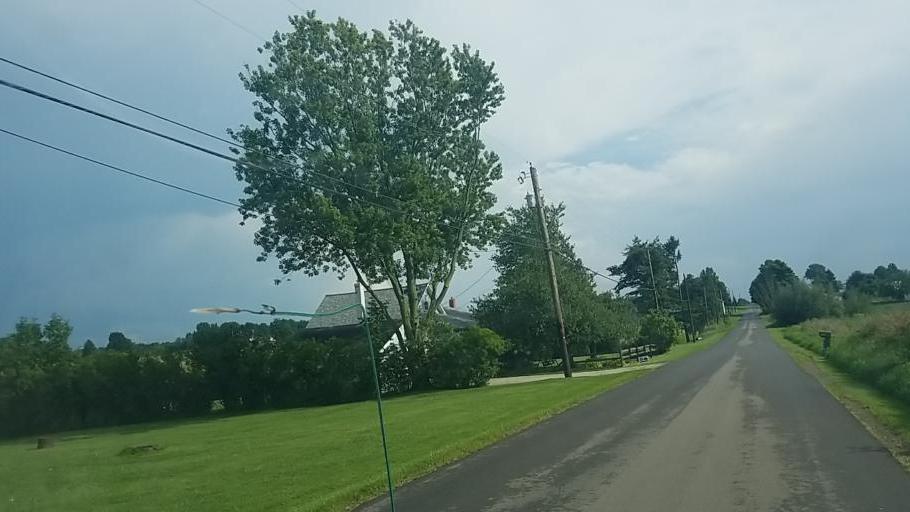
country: US
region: Ohio
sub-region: Wayne County
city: Creston
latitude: 40.9331
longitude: -81.9370
